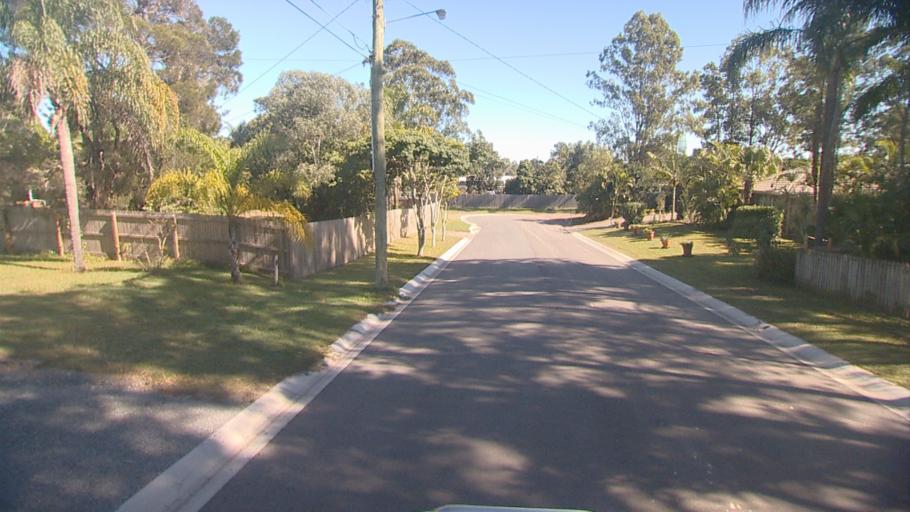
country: AU
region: Queensland
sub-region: Logan
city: Beenleigh
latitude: -27.6994
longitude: 153.2019
